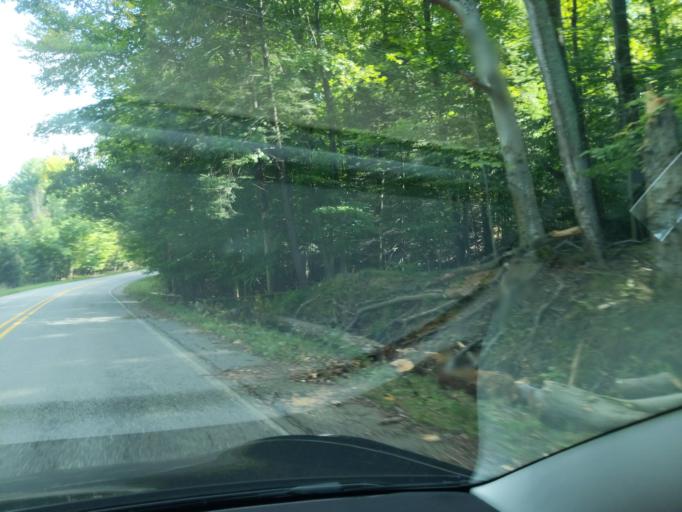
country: US
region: Michigan
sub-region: Antrim County
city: Bellaire
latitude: 45.0480
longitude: -85.3075
